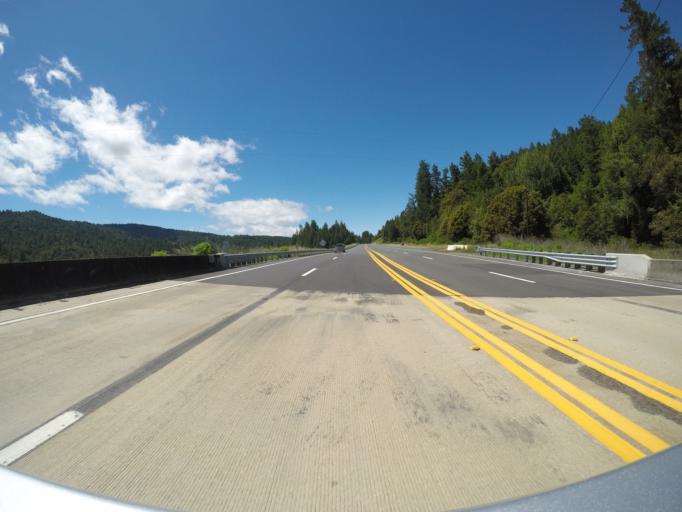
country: US
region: California
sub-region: Humboldt County
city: Redway
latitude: 39.9346
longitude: -123.7707
